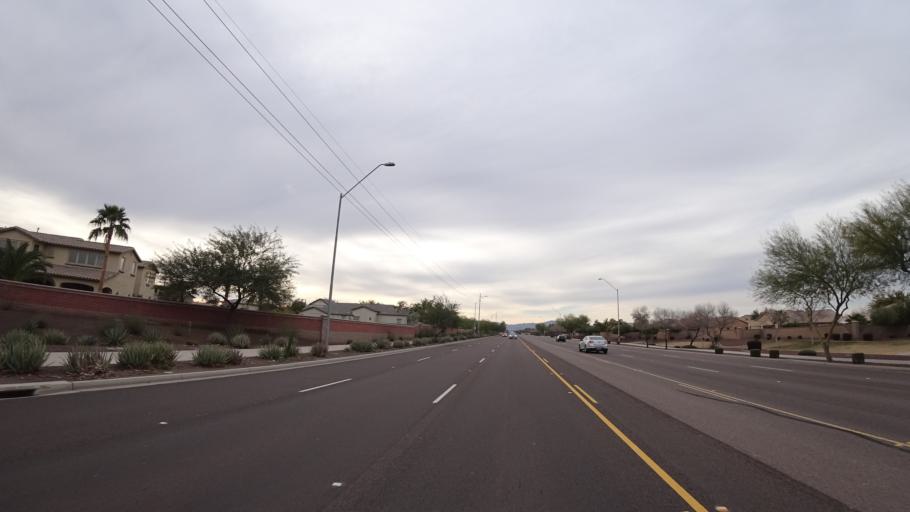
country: US
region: Arizona
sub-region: Maricopa County
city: Surprise
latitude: 33.6094
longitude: -112.3854
